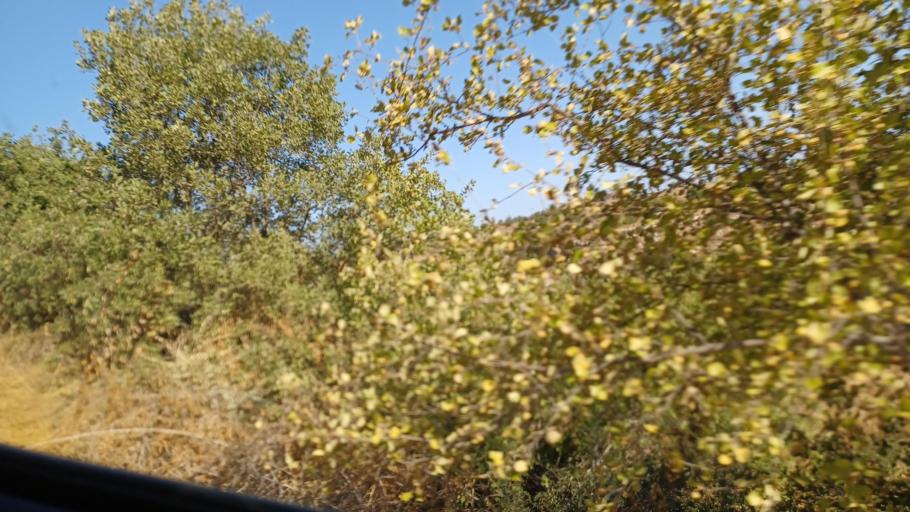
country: CY
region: Pafos
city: Polis
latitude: 34.9656
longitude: 32.4315
